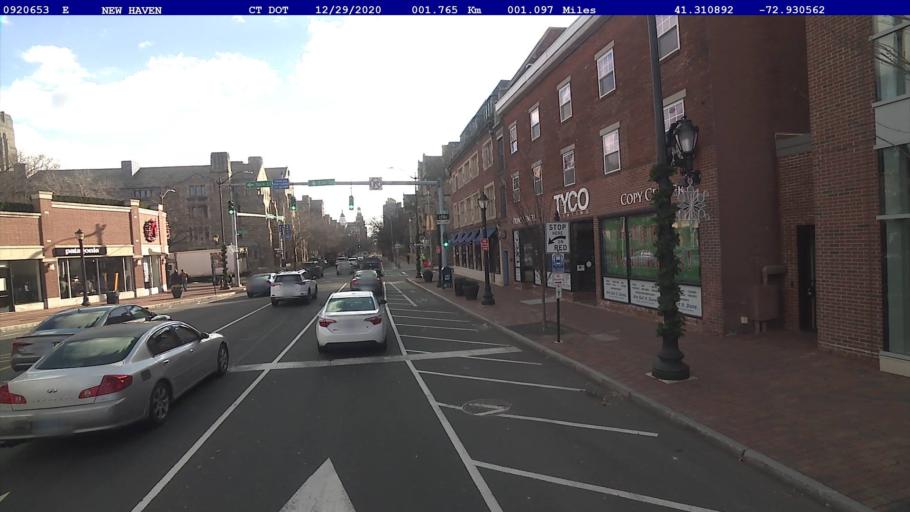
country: US
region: Connecticut
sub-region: New Haven County
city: New Haven
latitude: 41.3109
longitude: -72.9306
